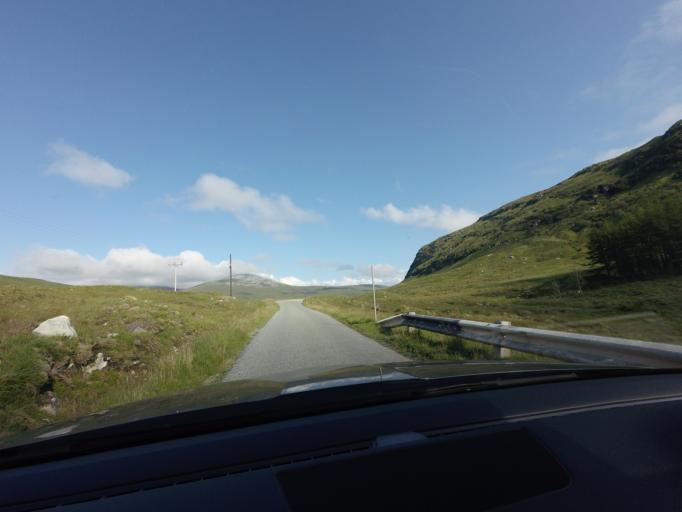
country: GB
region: Scotland
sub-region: Highland
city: Ullapool
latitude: 58.2569
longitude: -4.7910
